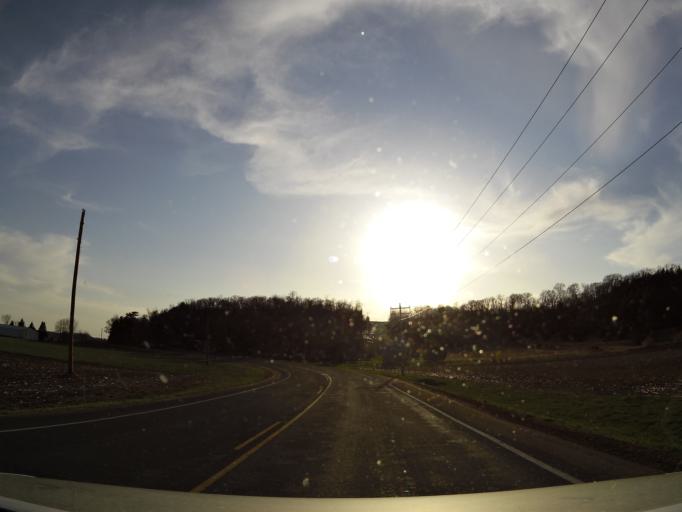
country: US
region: Wisconsin
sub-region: Pierce County
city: River Falls
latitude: 44.8769
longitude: -92.6617
